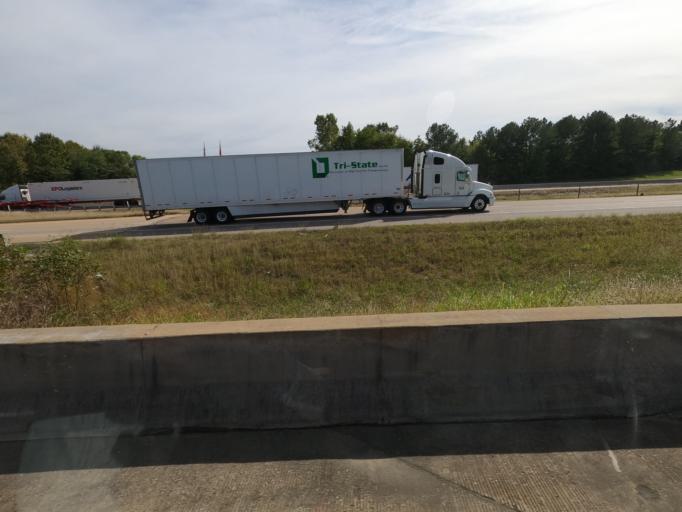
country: US
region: Tennessee
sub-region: Shelby County
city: Arlington
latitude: 35.2639
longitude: -89.6629
